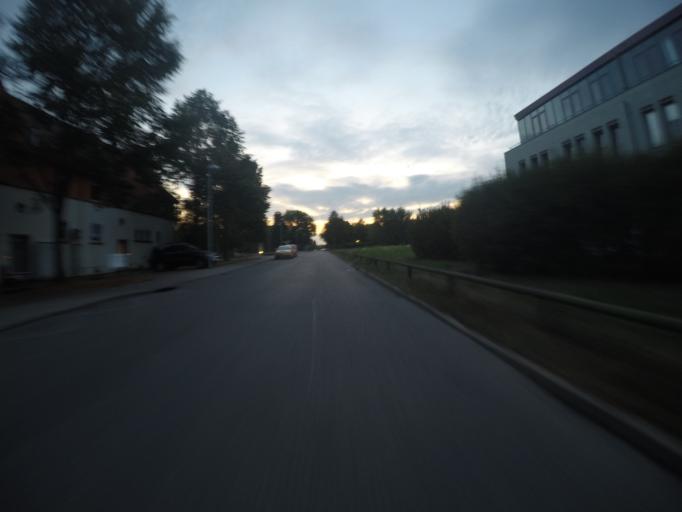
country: DE
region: Baden-Wuerttemberg
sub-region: Regierungsbezirk Stuttgart
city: Ostfildern
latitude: 48.7133
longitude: 9.2082
